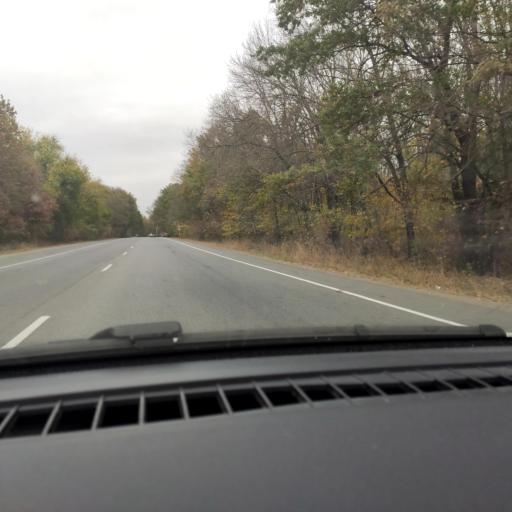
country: RU
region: Voronezj
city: Devitsa
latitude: 51.6292
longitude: 38.9911
